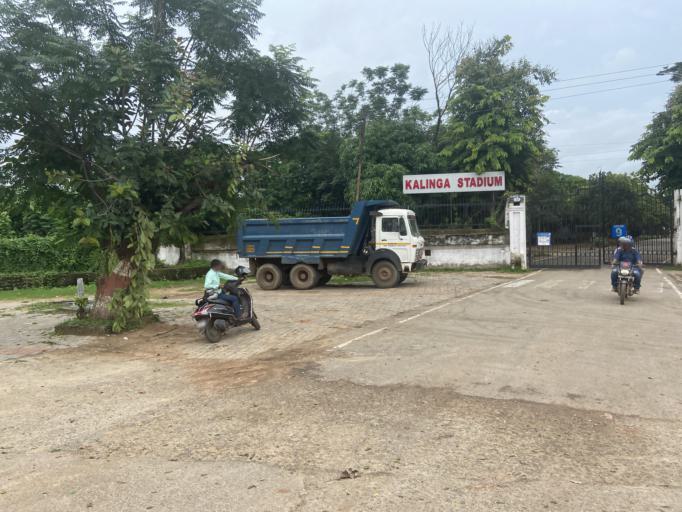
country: IN
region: Odisha
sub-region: Khordha
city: Bhubaneshwar
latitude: 20.2926
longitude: 85.8208
